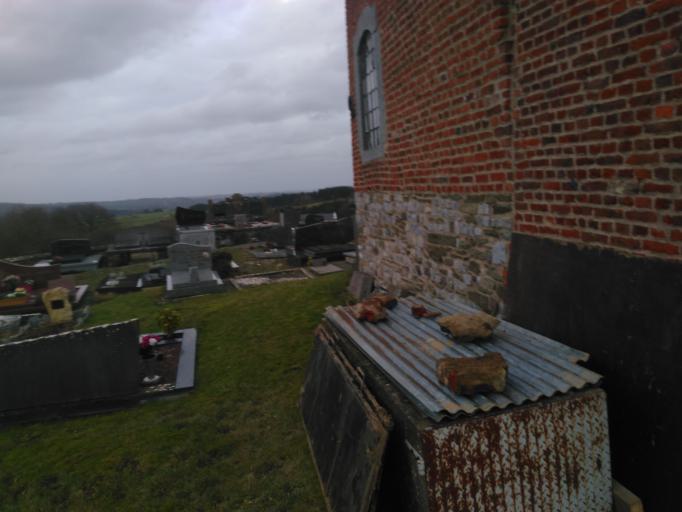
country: BE
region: Wallonia
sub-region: Province de Namur
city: Houyet
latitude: 50.1536
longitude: 5.0317
